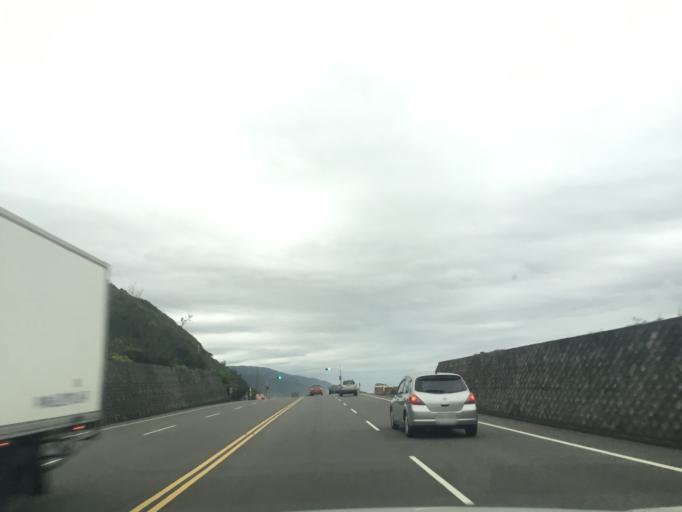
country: TW
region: Taiwan
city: Hengchun
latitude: 22.3094
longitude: 120.8905
